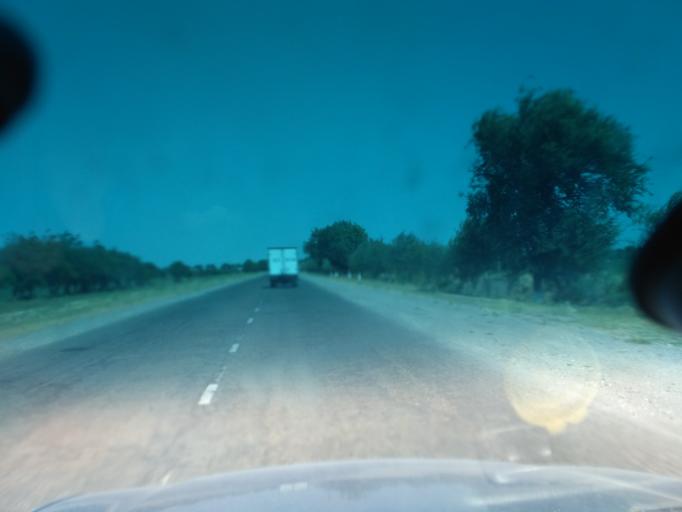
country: UZ
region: Sirdaryo
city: Guliston
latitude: 40.4869
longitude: 68.8903
